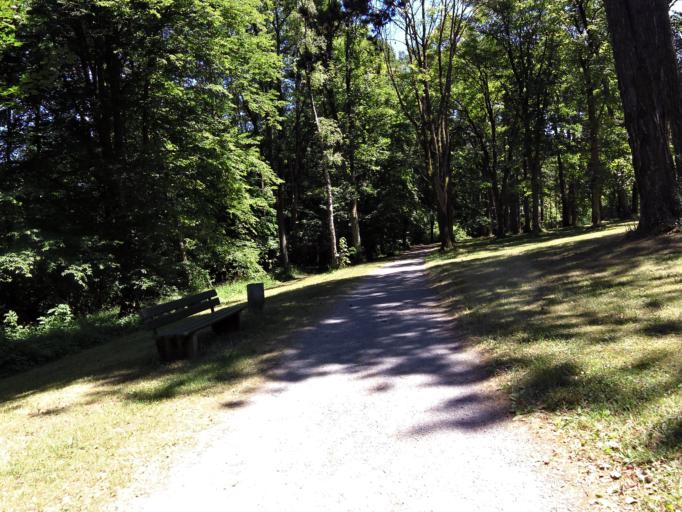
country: DE
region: Bavaria
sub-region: Regierungsbezirk Unterfranken
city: Hochberg
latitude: 49.7825
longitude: 9.9107
